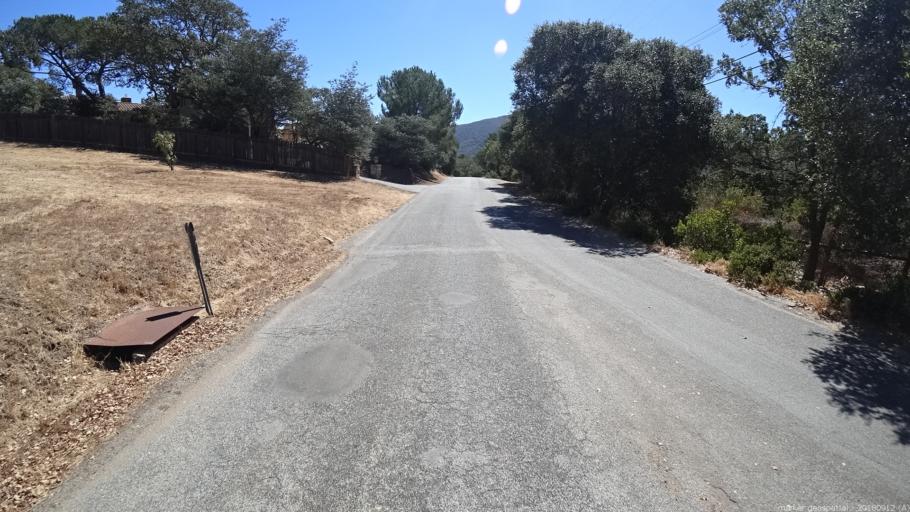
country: US
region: California
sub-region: Monterey County
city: Carmel Valley Village
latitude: 36.4976
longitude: -121.7470
